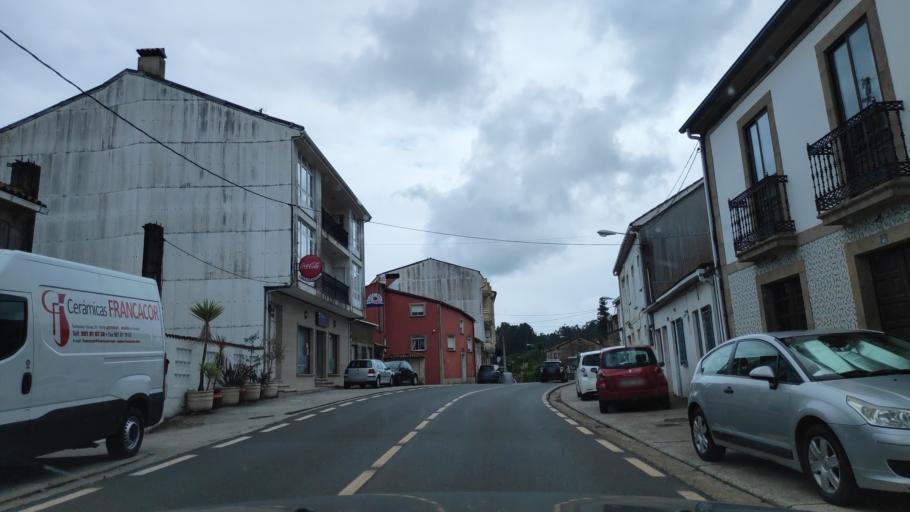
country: ES
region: Galicia
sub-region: Provincia da Coruna
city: Padron
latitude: 42.7315
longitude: -8.6702
